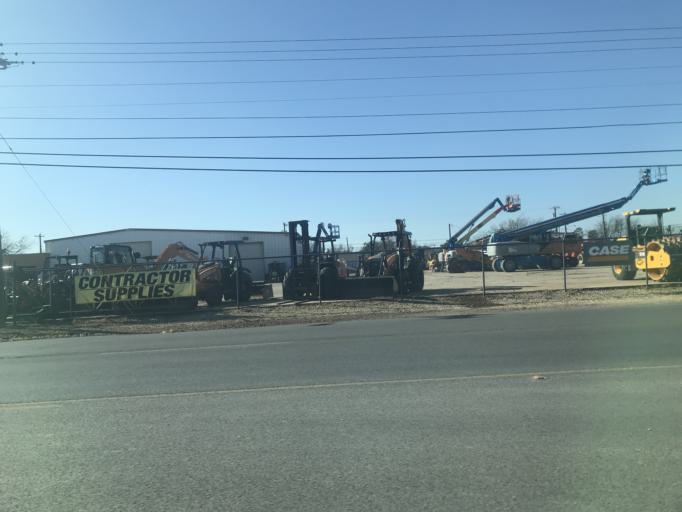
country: US
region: Texas
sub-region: Taylor County
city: Abilene
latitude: 32.4135
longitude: -99.7424
